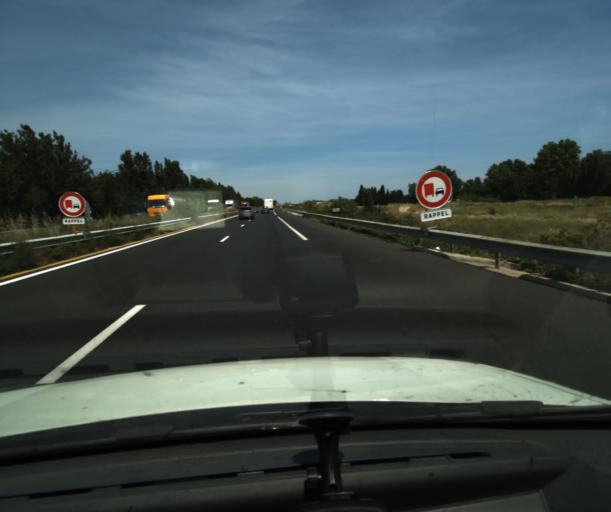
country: FR
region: Languedoc-Roussillon
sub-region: Departement des Pyrenees-Orientales
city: Saint-Esteve
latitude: 42.7051
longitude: 2.8659
